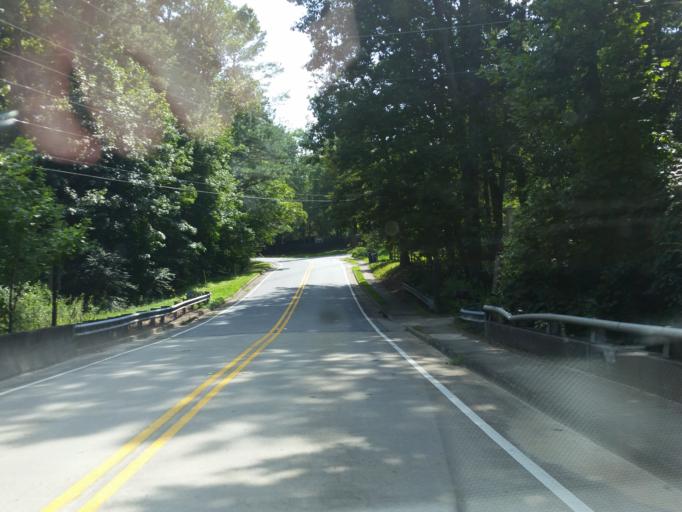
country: US
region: Georgia
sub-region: Fulton County
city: Roswell
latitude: 34.0203
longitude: -84.4535
